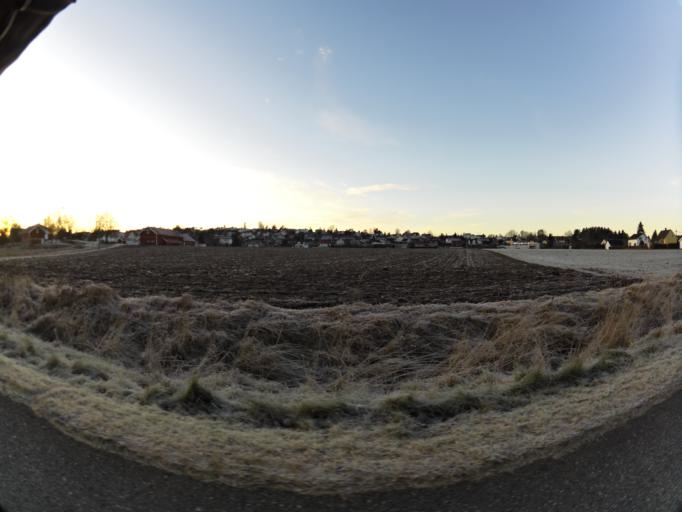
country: NO
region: Ostfold
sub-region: Fredrikstad
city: Fredrikstad
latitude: 59.2636
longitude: 11.0132
